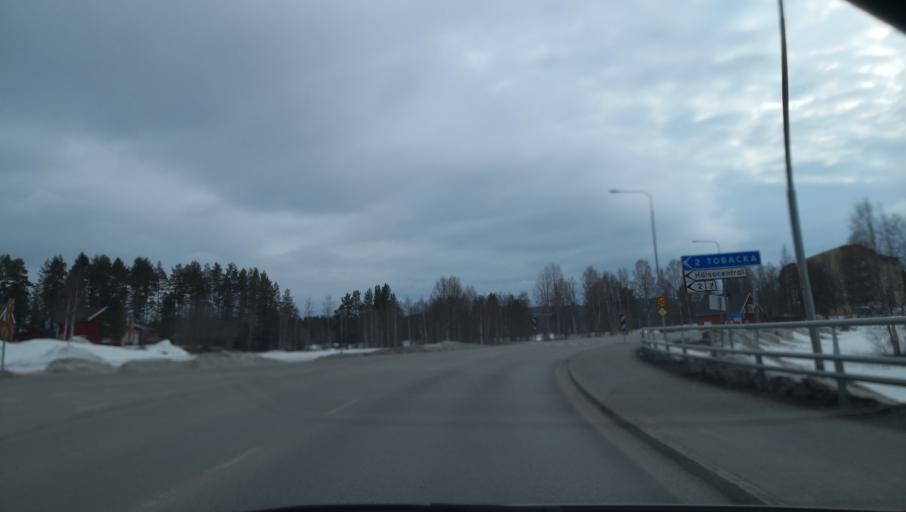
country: SE
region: Vaesterbotten
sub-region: Vannas Kommun
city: Vaennaes
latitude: 63.9089
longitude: 19.7704
